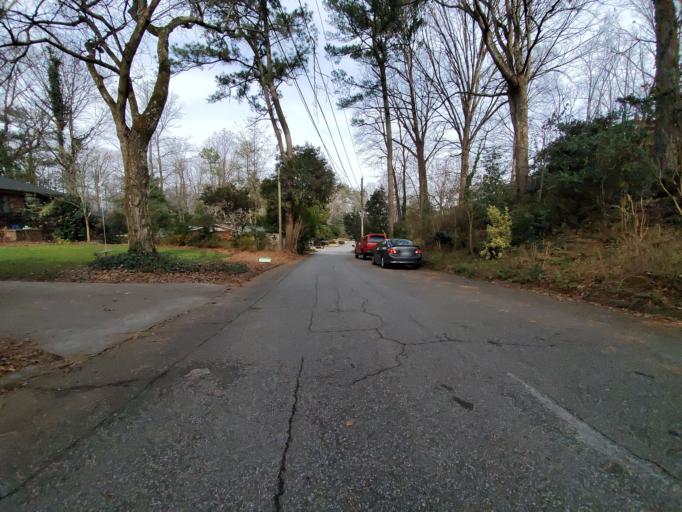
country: US
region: Georgia
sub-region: DeKalb County
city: North Decatur
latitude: 33.7822
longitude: -84.3148
